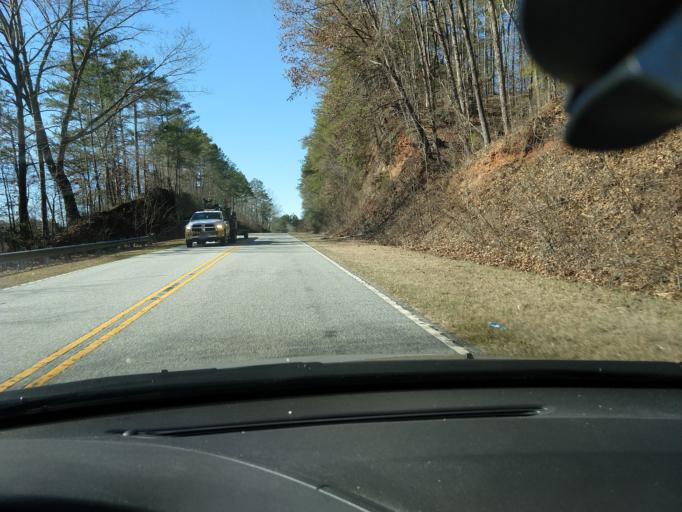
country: US
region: Georgia
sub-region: Stephens County
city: Toccoa
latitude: 34.6125
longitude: -83.2116
